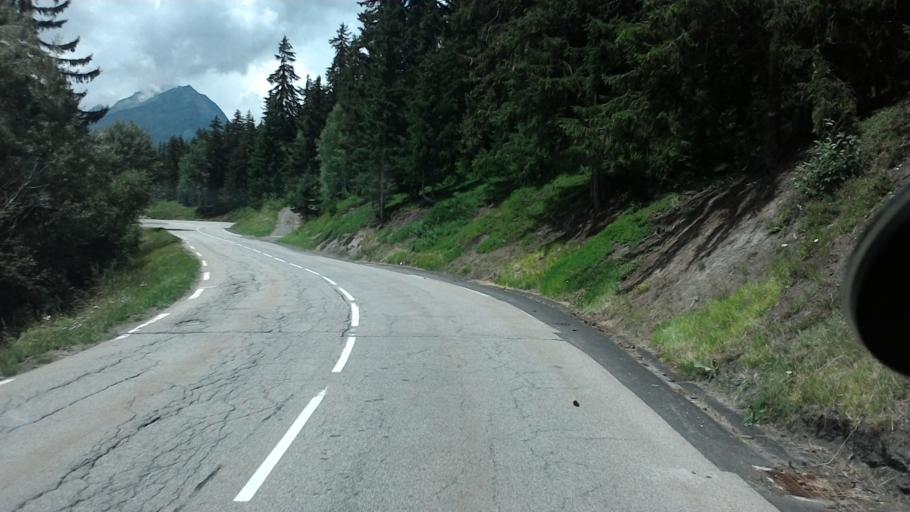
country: FR
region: Rhone-Alpes
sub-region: Departement de la Savoie
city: Seez
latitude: 45.6224
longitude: 6.8453
